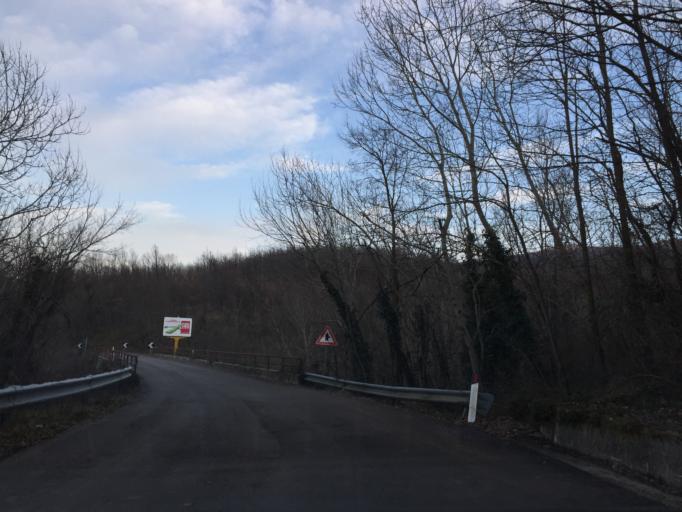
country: IT
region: Molise
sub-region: Provincia di Campobasso
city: Guardiaregia
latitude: 41.4408
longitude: 14.5463
